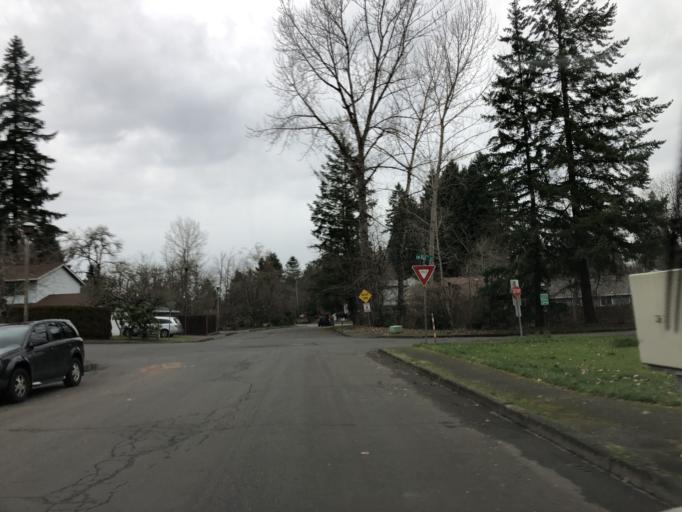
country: US
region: Oregon
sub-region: Washington County
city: Tigard
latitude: 45.4274
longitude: -122.7878
